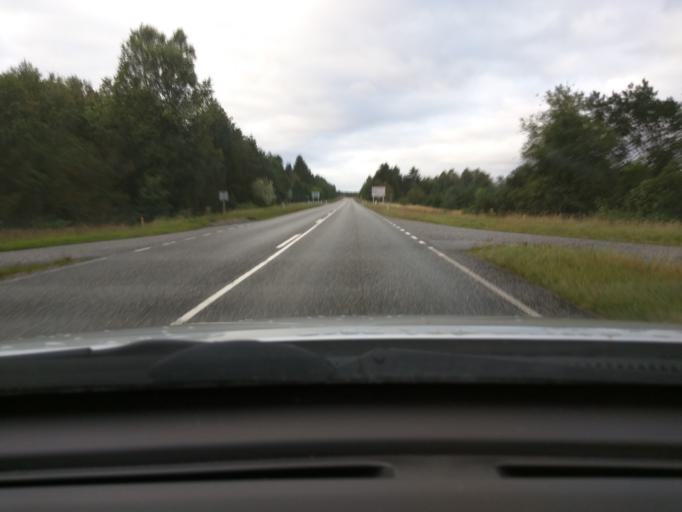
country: DK
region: Central Jutland
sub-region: Ikast-Brande Kommune
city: Bording Kirkeby
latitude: 56.1995
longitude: 9.3156
